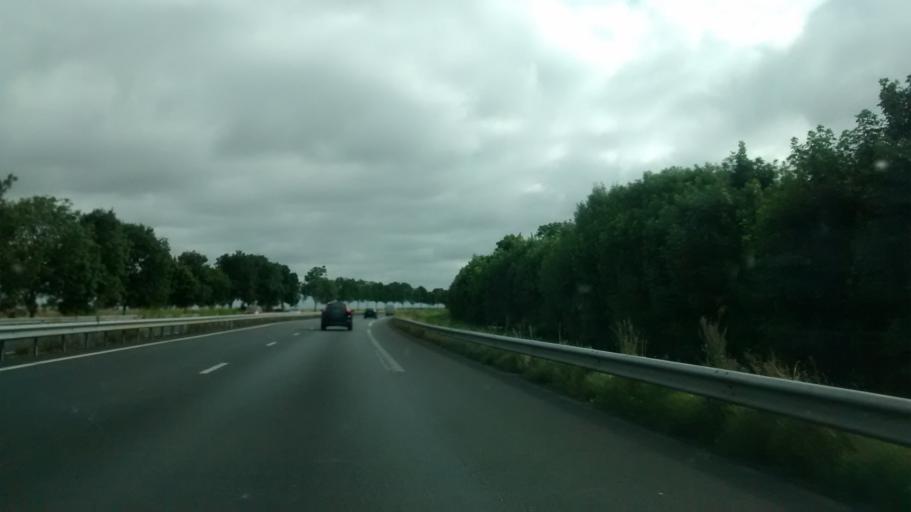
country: FR
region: Lower Normandy
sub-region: Departement du Calvados
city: Tourville-sur-Odon
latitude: 49.1508
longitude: -0.5039
